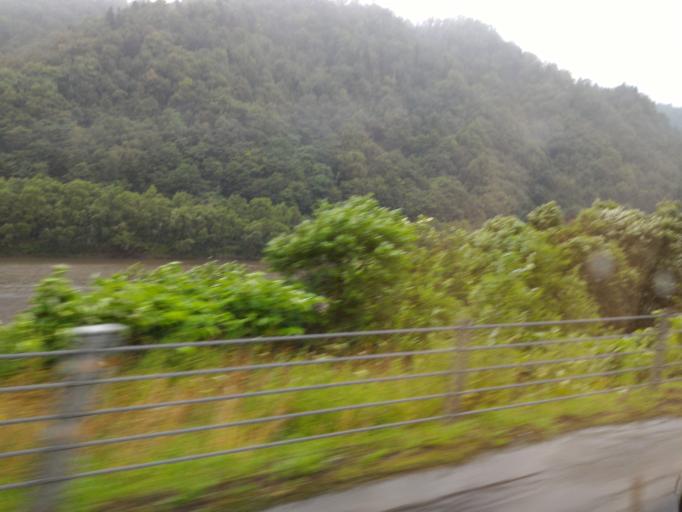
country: JP
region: Hokkaido
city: Nayoro
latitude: 44.7395
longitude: 142.1164
